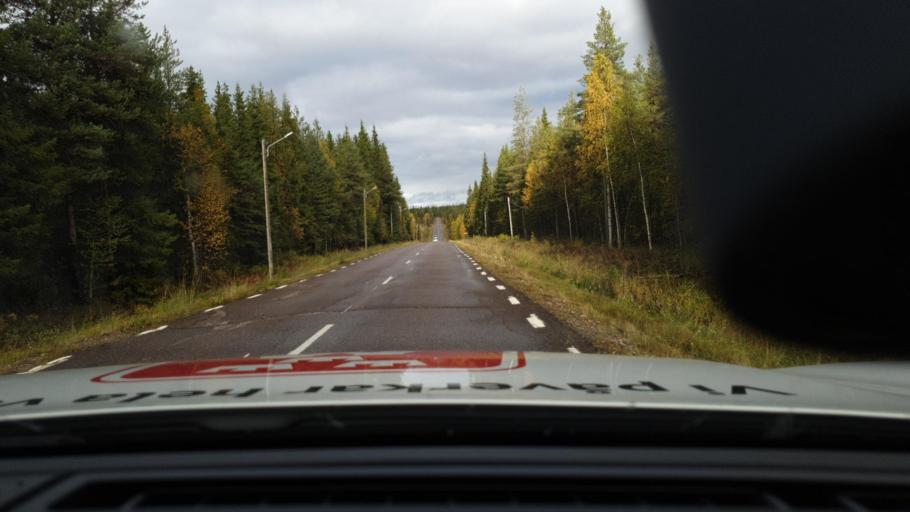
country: SE
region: Norrbotten
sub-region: Overkalix Kommun
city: OEverkalix
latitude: 67.0048
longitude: 22.5123
